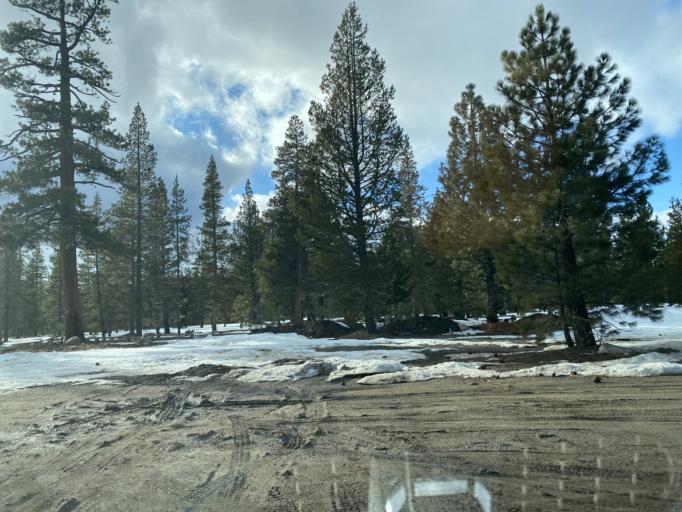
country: US
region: California
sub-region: El Dorado County
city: South Lake Tahoe
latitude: 38.8505
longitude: -120.0203
